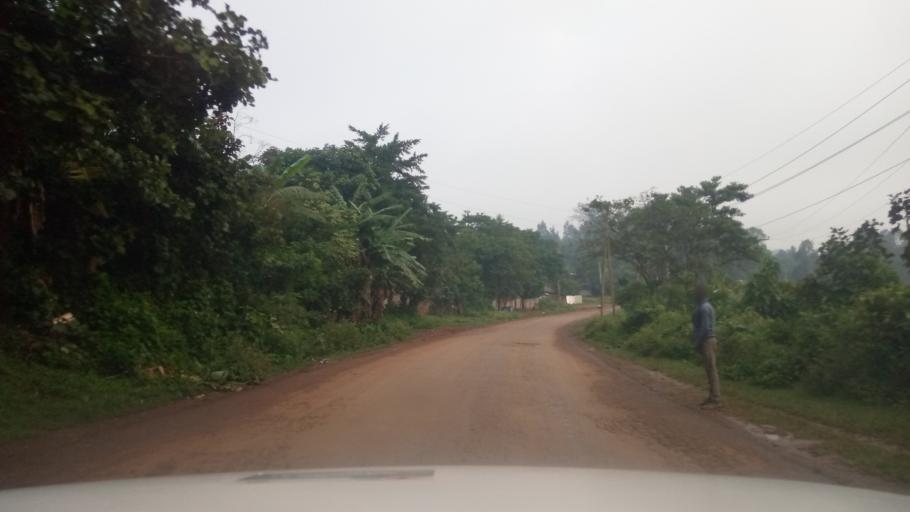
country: ET
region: Oromiya
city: Jima
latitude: 7.6883
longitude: 36.8273
